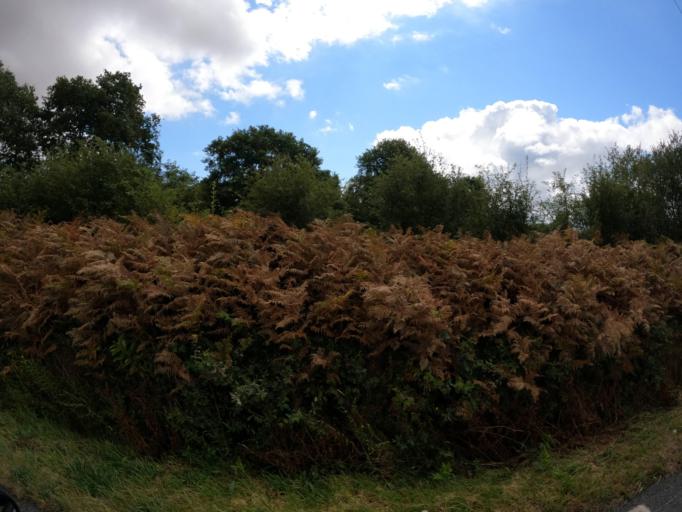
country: FR
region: Pays de la Loire
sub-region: Departement de la Loire-Atlantique
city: Vallet
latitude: 47.1969
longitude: -1.2484
